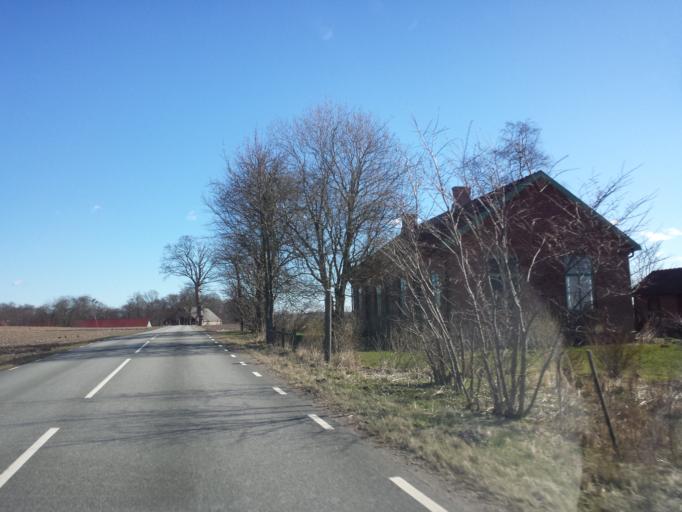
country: SE
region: Skane
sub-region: Sjobo Kommun
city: Sjoebo
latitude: 55.6210
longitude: 13.8296
